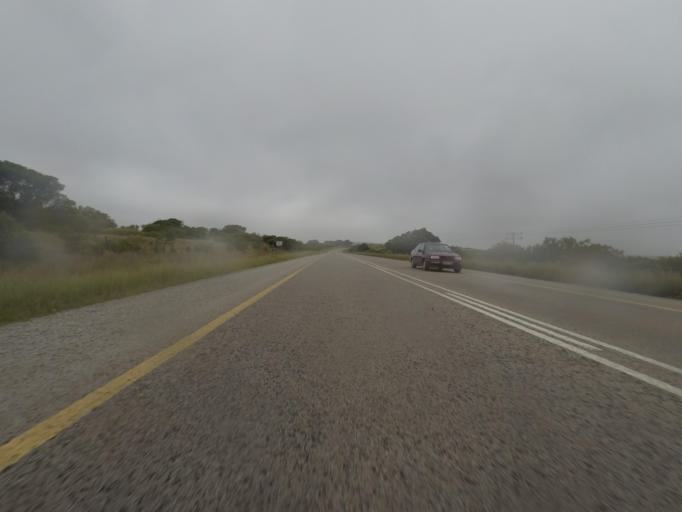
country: ZA
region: Eastern Cape
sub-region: Cacadu District Municipality
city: Grahamstown
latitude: -33.6428
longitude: 26.3640
